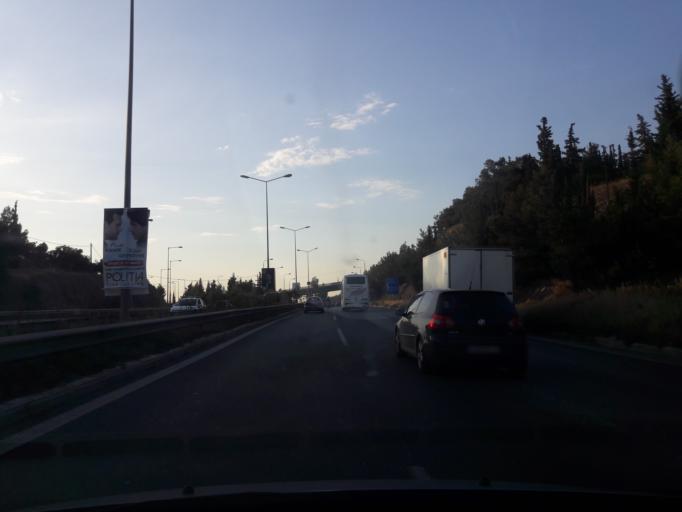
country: GR
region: Central Macedonia
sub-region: Nomos Thessalonikis
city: Agios Pavlos
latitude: 40.6405
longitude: 22.9699
